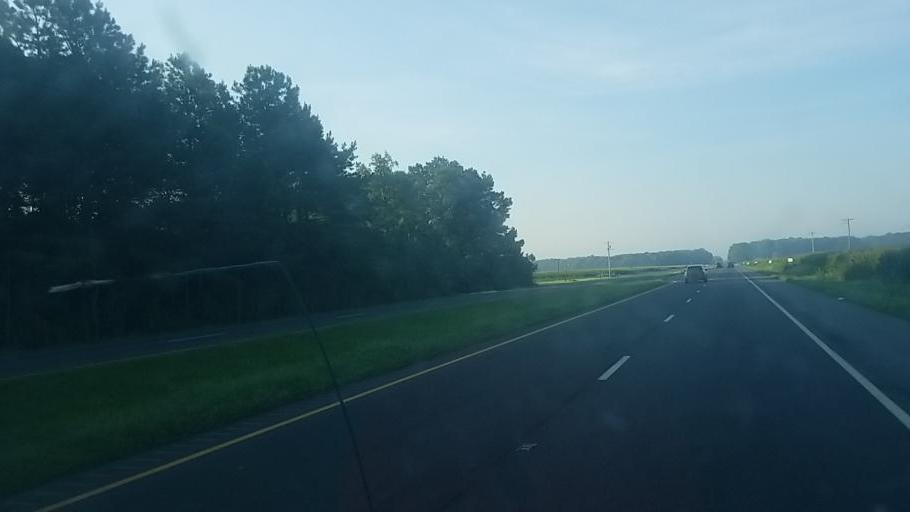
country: US
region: Delaware
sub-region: Sussex County
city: Selbyville
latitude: 38.4965
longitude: -75.2370
